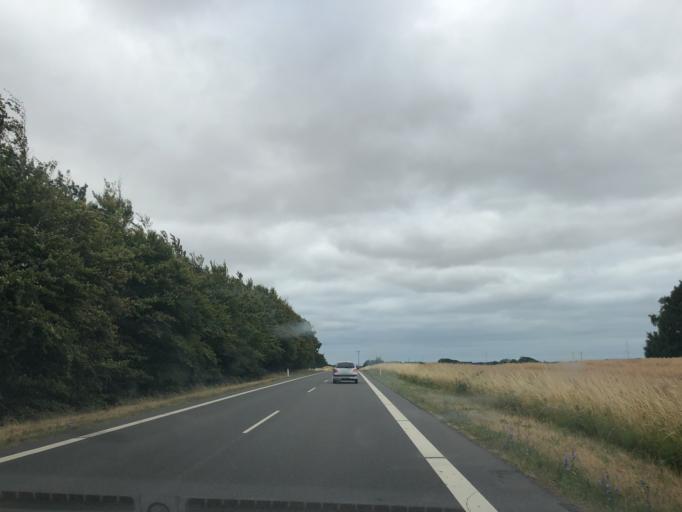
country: DK
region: Zealand
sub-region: Slagelse Kommune
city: Skaelskor
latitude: 55.2428
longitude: 11.3191
